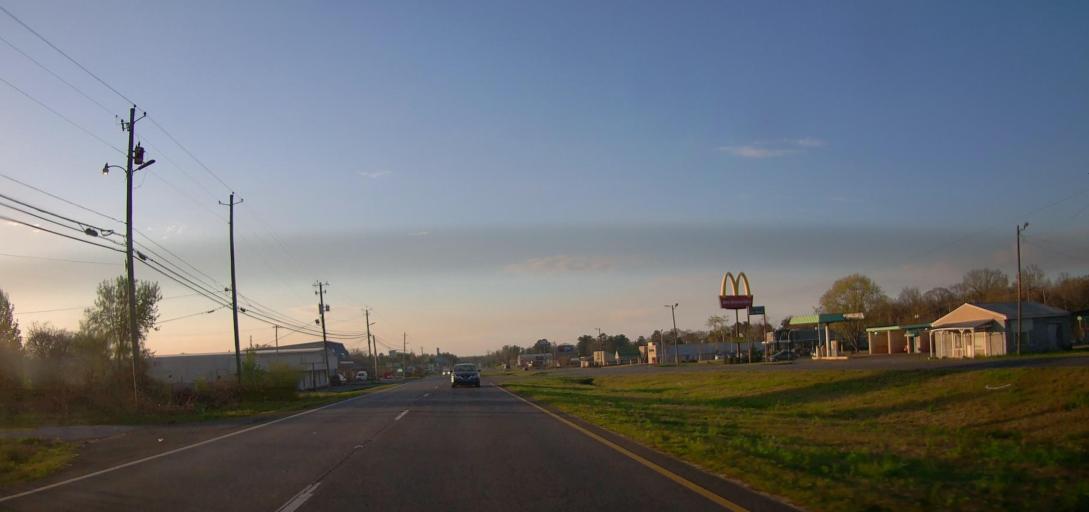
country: US
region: Alabama
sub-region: Talladega County
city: Childersburg
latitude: 33.2632
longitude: -86.3499
